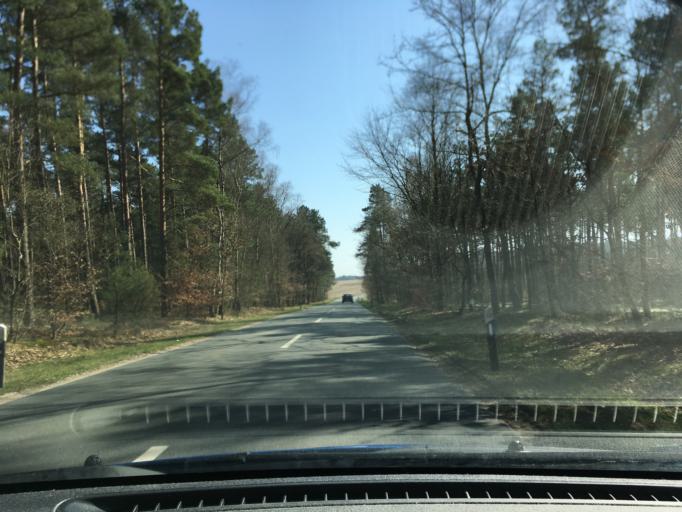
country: DE
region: Lower Saxony
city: Eimke
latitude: 52.9911
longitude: 10.3052
